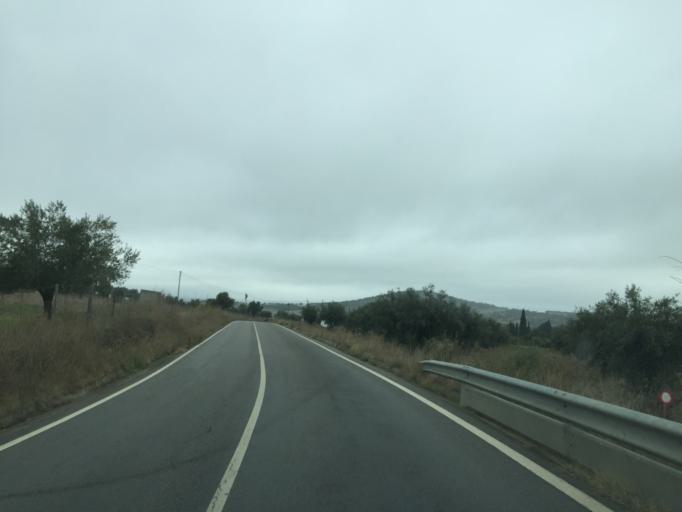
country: PT
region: Portalegre
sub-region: Alter do Chao
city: Alter do Chao
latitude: 39.2128
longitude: -7.6554
